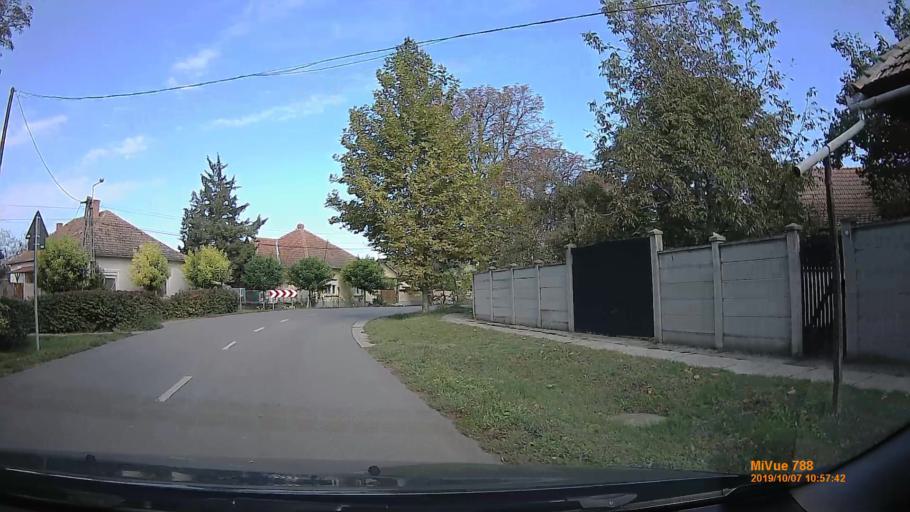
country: HU
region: Bekes
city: Kondoros
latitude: 46.7558
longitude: 20.7977
